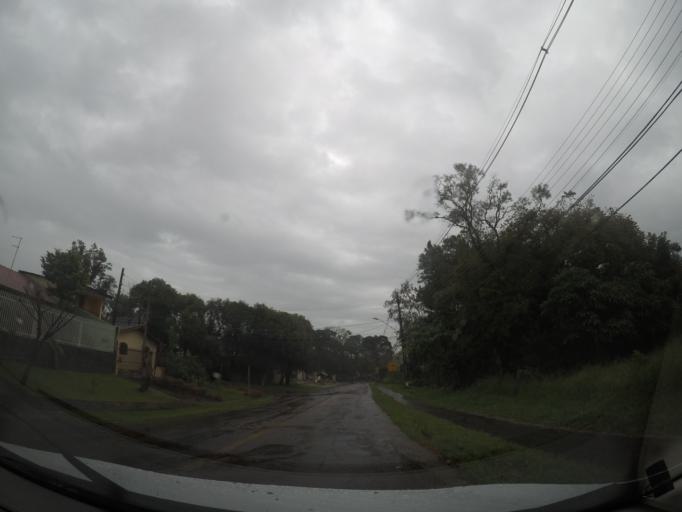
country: BR
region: Parana
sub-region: Curitiba
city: Curitiba
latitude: -25.4541
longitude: -49.3790
